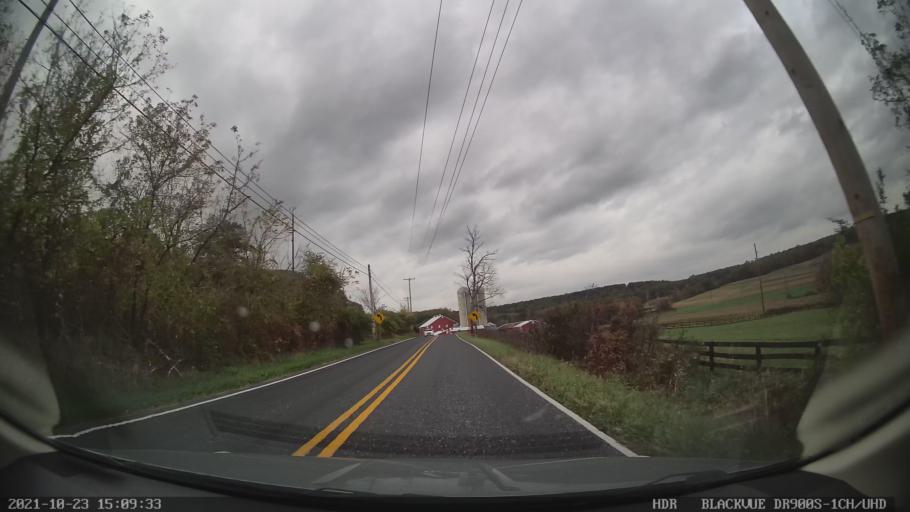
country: US
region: Pennsylvania
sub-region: Berks County
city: Red Lion
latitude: 40.4496
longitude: -75.6313
